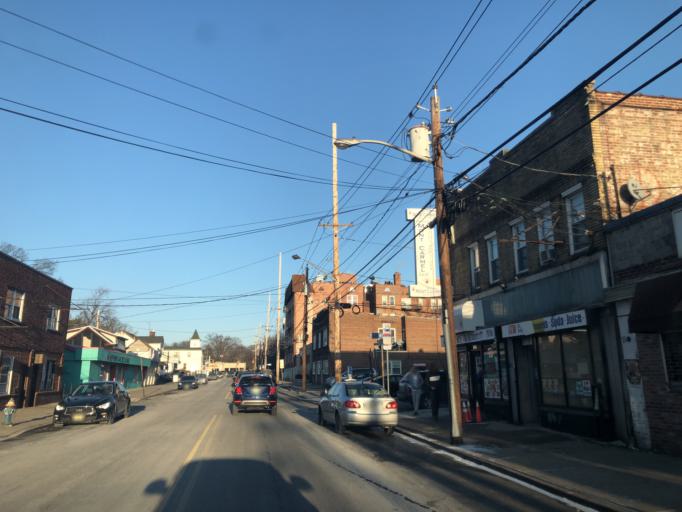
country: US
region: New Jersey
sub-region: Union County
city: Union
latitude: 40.7136
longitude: -74.2548
